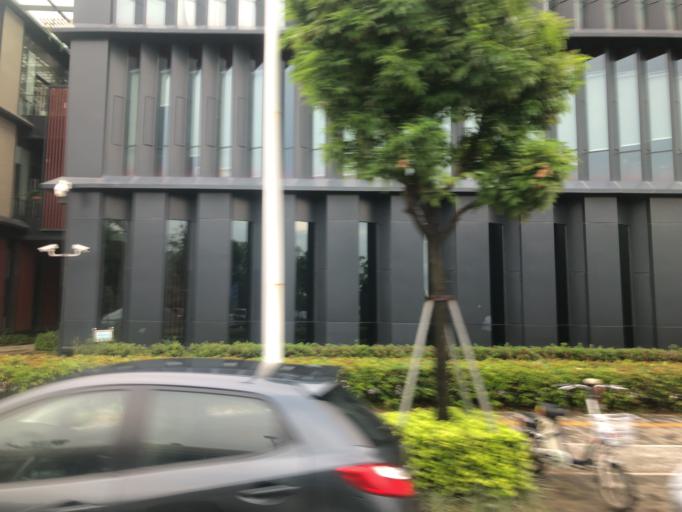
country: CN
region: Guangdong
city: Nantou
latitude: 22.5191
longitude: 113.8953
